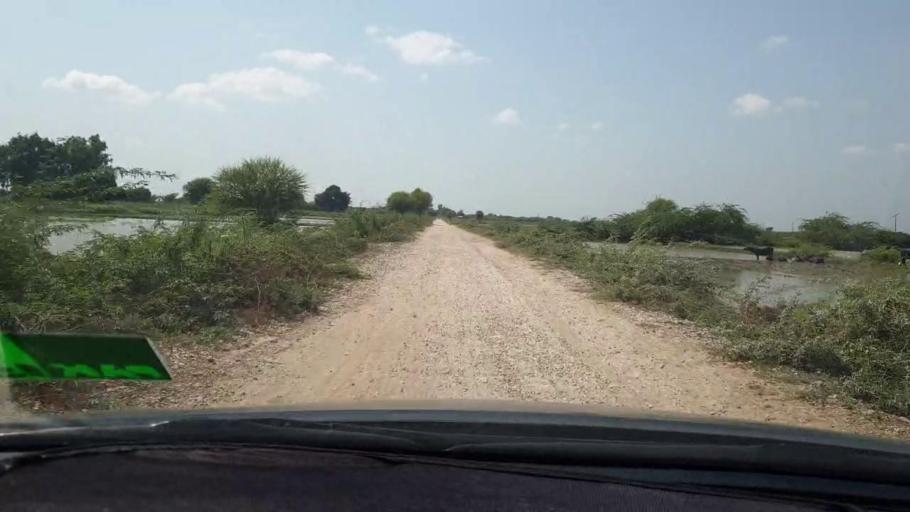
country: PK
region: Sindh
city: Naukot
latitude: 24.9149
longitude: 69.2686
